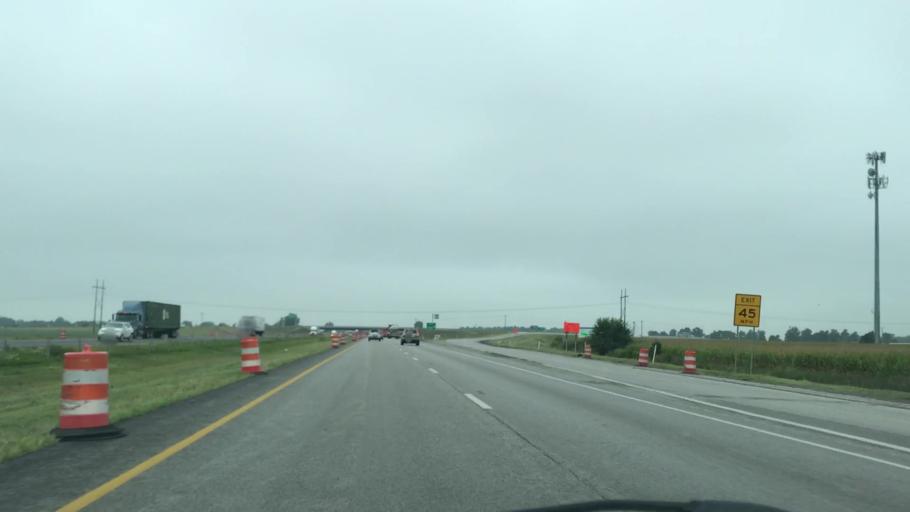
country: US
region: Indiana
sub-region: Clinton County
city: Mulberry
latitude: 40.2579
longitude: -86.6509
